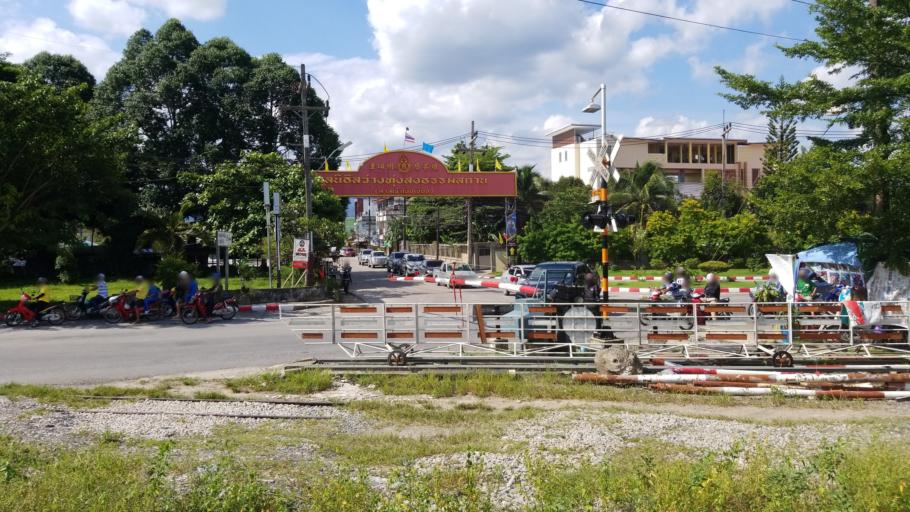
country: TH
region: Nakhon Si Thammarat
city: Thung Song
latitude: 8.1668
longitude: 99.6830
